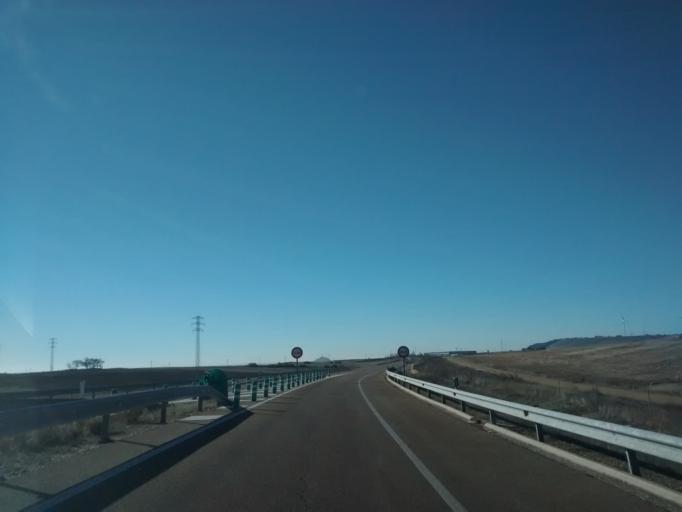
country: ES
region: Castille and Leon
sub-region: Provincia de Palencia
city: Fuentes de Valdepero
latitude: 42.0593
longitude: -4.4949
